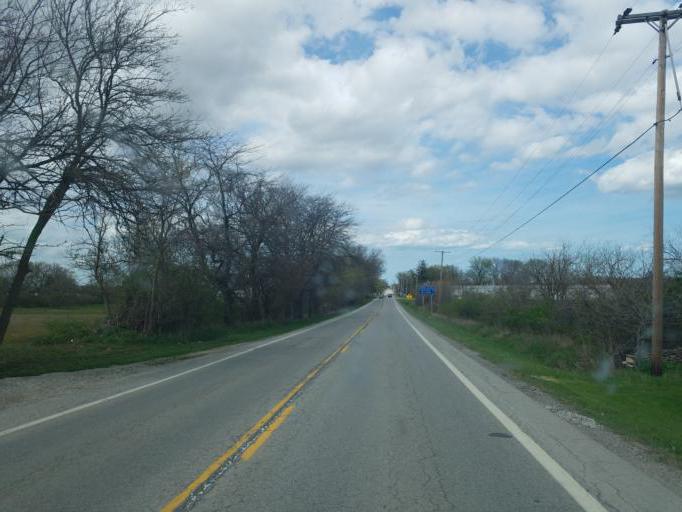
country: US
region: Ohio
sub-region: Erie County
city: Sandusky
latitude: 41.3582
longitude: -82.7508
